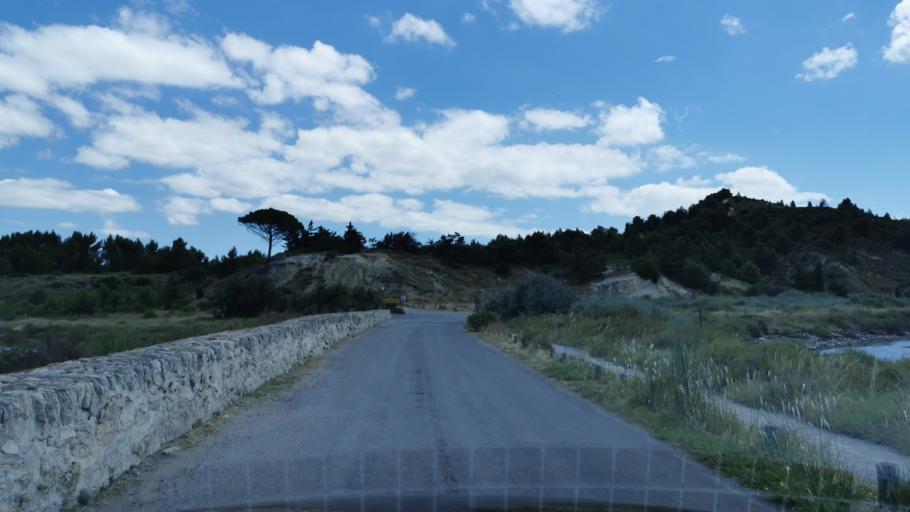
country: FR
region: Languedoc-Roussillon
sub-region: Departement de l'Aude
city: Peyriac-de-Mer
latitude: 43.0858
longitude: 2.9669
